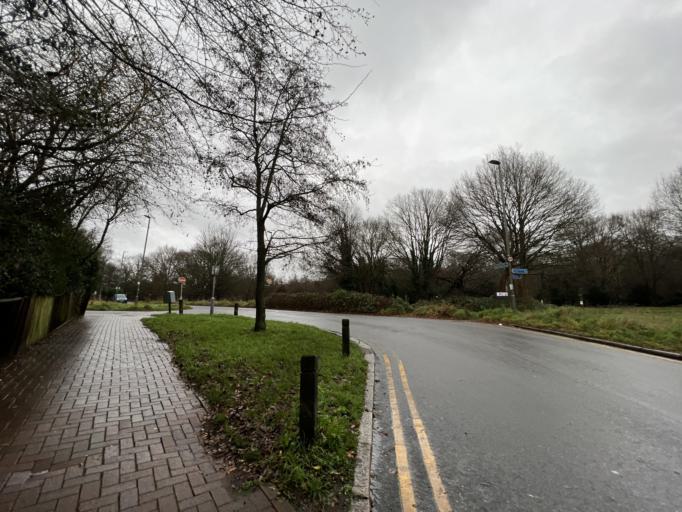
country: GB
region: England
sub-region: Greater London
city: Wandsworth
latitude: 51.4504
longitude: -0.2366
